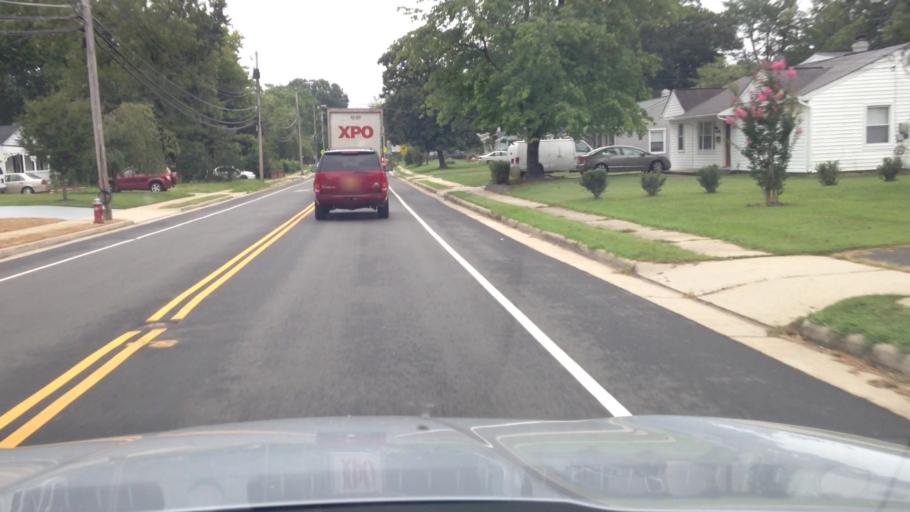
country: US
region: Virginia
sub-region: Fairfax County
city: Groveton
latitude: 38.7720
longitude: -77.0937
